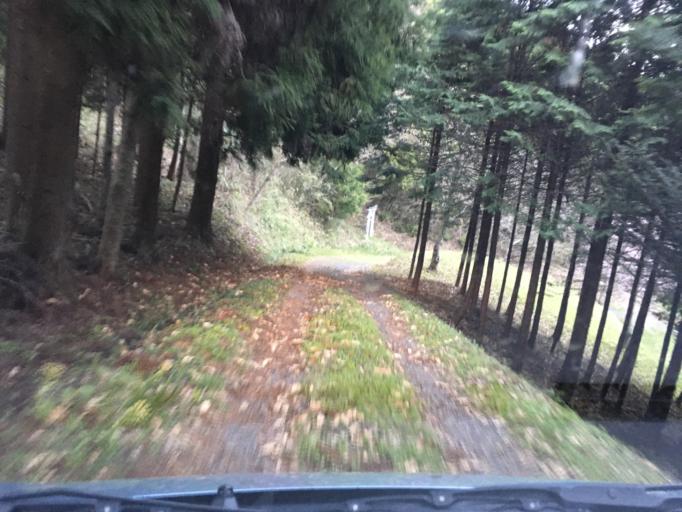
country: JP
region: Iwate
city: Ichinoseki
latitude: 38.9604
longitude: 141.2037
